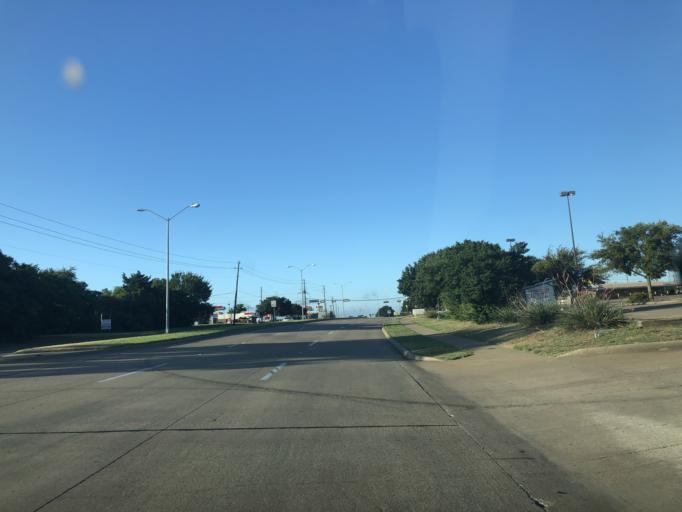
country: US
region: Texas
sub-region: Dallas County
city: Duncanville
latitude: 32.6346
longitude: -96.9430
